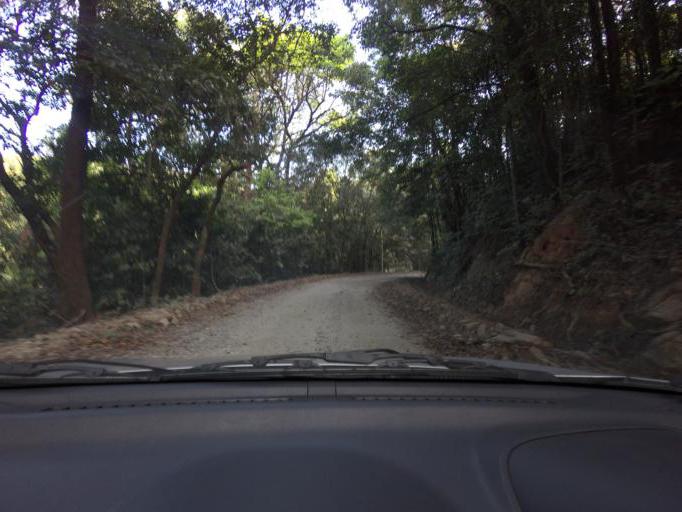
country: IN
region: Karnataka
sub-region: Kodagu
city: Somvarpet
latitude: 12.7111
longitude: 75.6882
